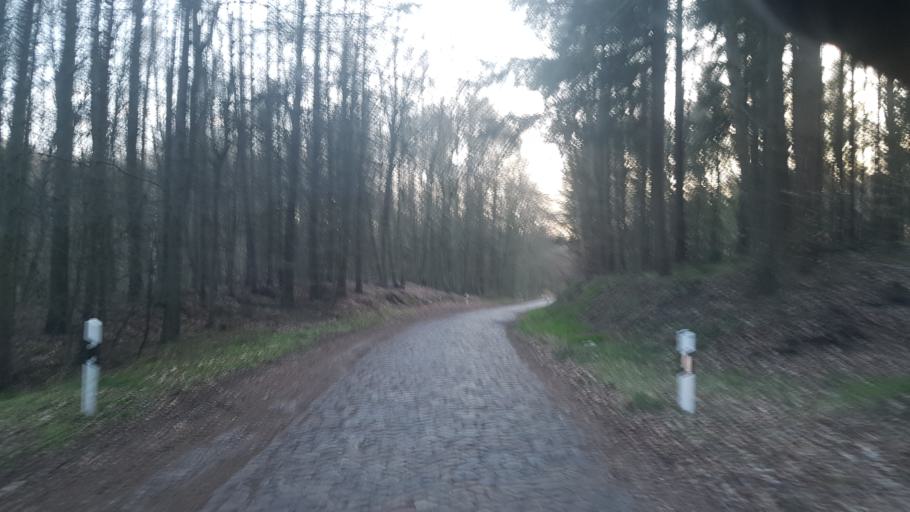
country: DE
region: Brandenburg
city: Gramzow
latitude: 53.1968
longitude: 13.9349
